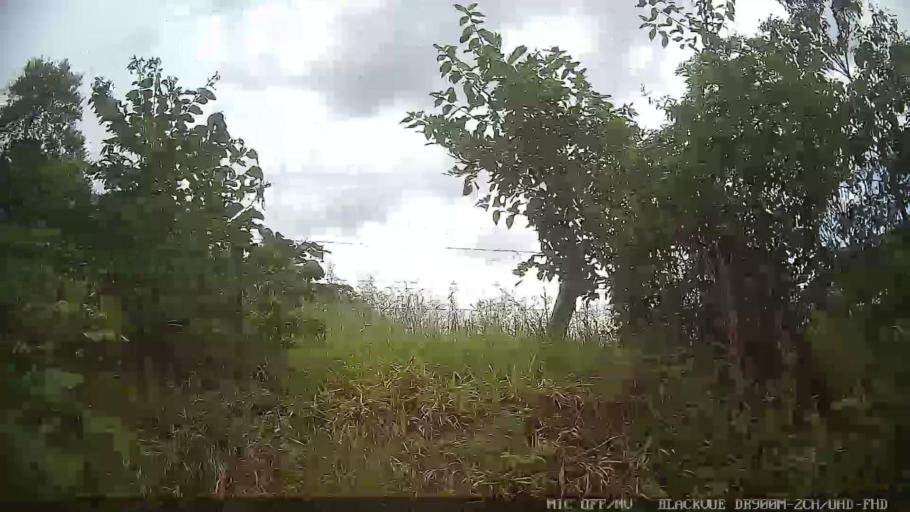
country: BR
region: Sao Paulo
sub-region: Atibaia
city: Atibaia
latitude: -23.1498
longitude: -46.5701
